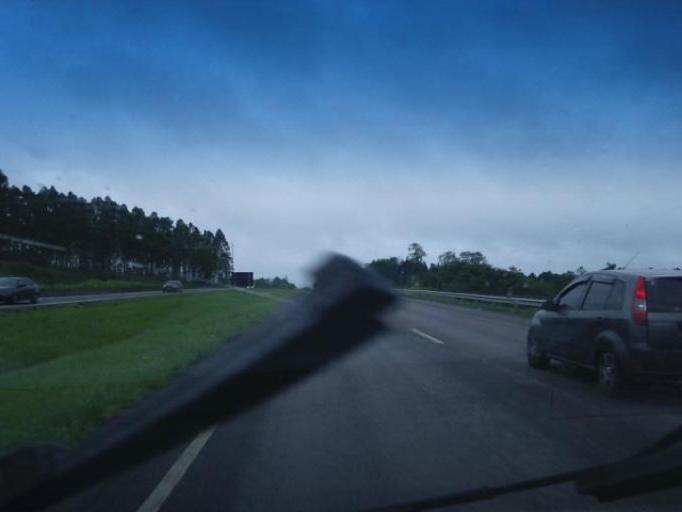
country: BR
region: Sao Paulo
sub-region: Registro
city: Registro
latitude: -24.4744
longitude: -47.8262
